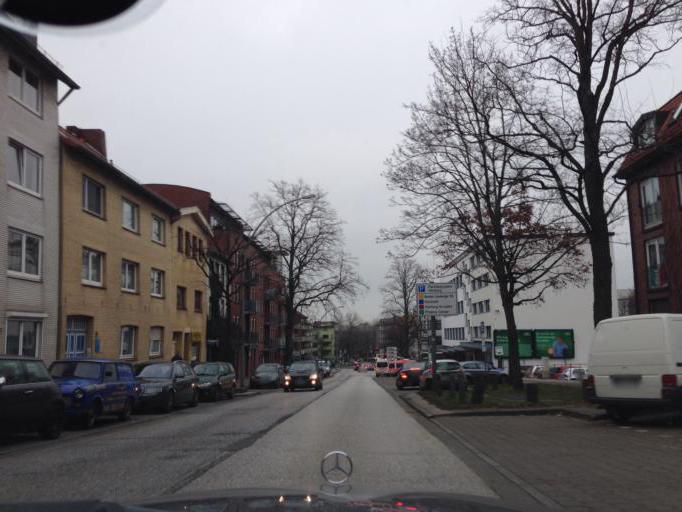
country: DE
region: Hamburg
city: Harburg
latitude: 53.4624
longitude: 9.9746
